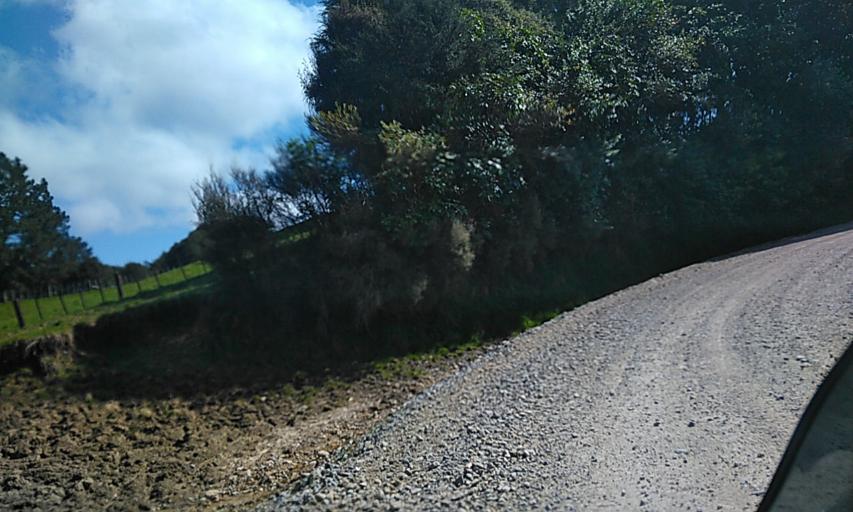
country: NZ
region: Gisborne
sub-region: Gisborne District
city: Gisborne
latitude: -38.2115
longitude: 178.0650
